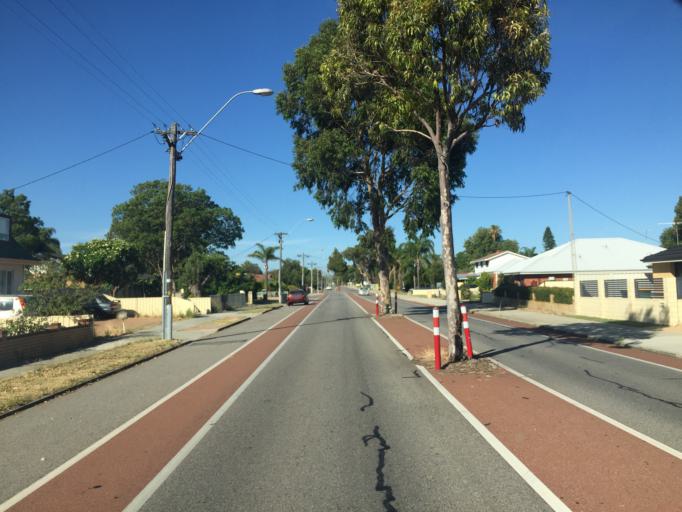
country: AU
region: Western Australia
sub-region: Canning
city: East Cannington
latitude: -32.0169
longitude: 115.9615
